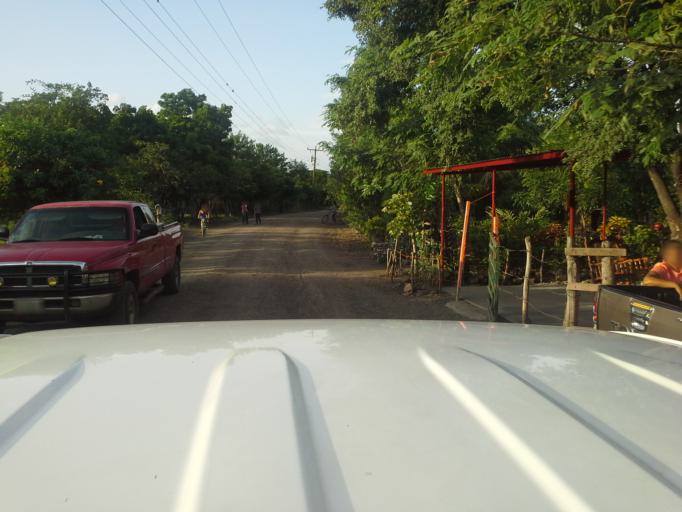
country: NI
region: Matagalpa
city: Ciudad Dario
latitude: 12.7987
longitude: -86.1452
